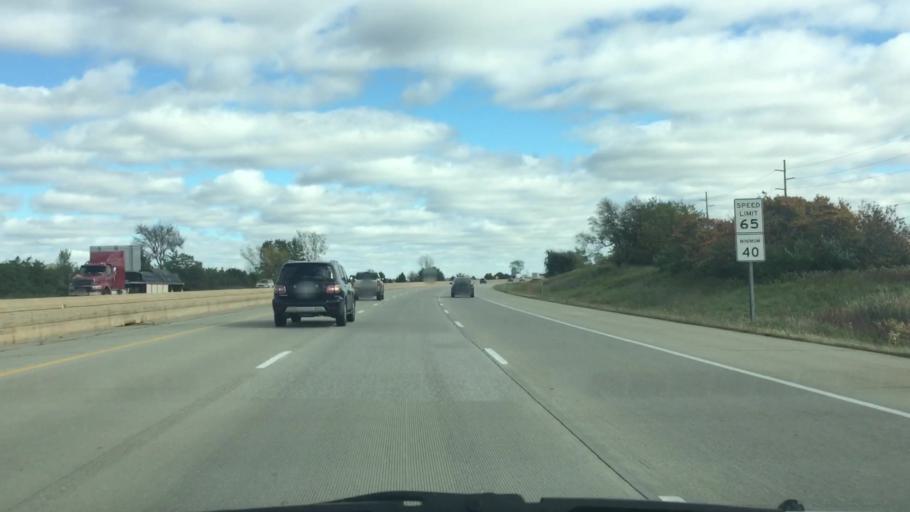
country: US
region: Iowa
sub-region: Johnson County
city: Iowa City
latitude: 41.6861
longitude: -91.4869
